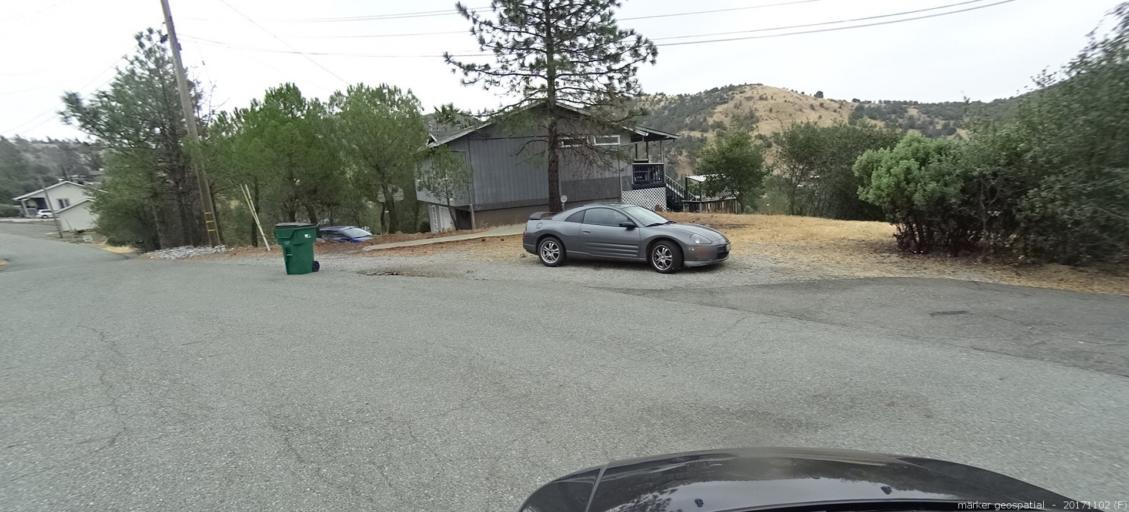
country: US
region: California
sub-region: Shasta County
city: Bella Vista
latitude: 40.7190
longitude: -122.2386
